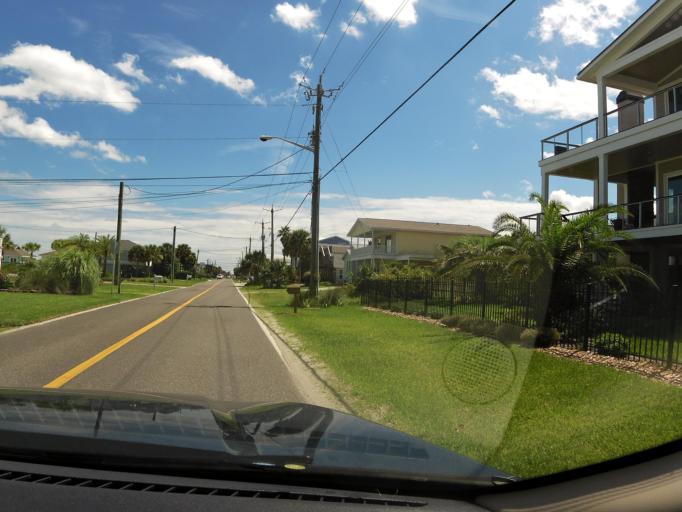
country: US
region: Florida
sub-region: Nassau County
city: Fernandina Beach
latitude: 30.6730
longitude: -81.4309
